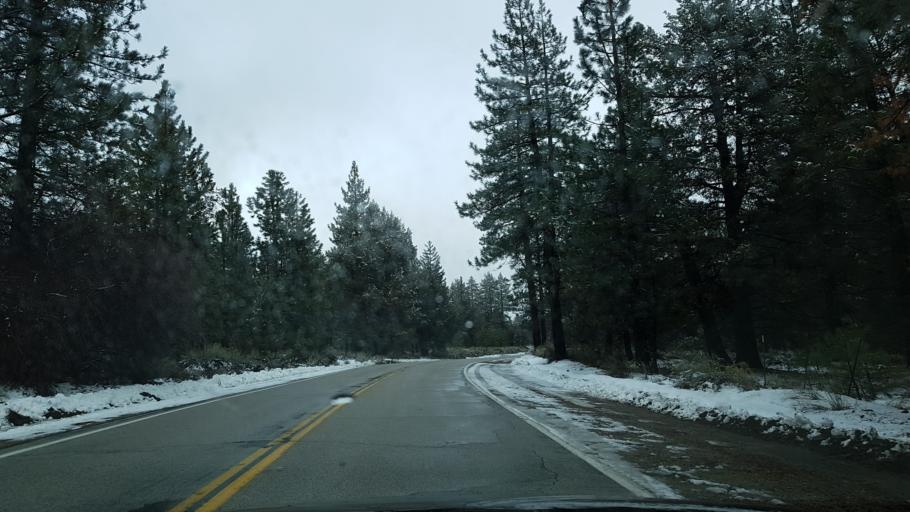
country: US
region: California
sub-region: San Bernardino County
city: Big Bear Lake
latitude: 34.2621
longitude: -116.9163
